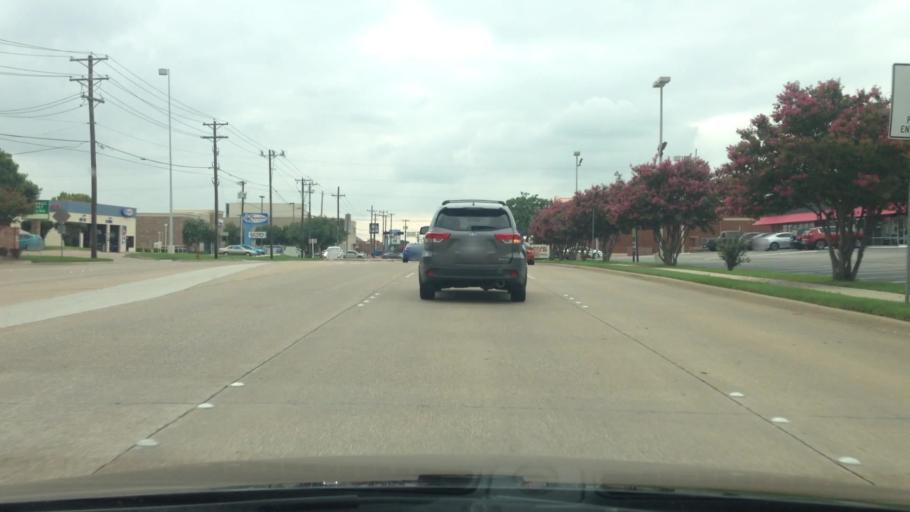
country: US
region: Texas
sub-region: Tarrant County
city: Watauga
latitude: 32.8605
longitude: -97.2357
